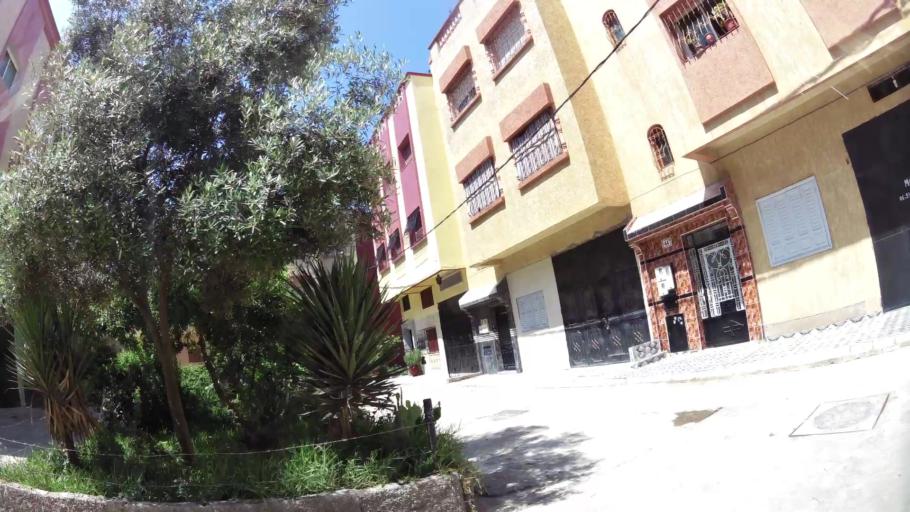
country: MA
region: Rabat-Sale-Zemmour-Zaer
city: Sale
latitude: 34.0782
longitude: -6.7872
